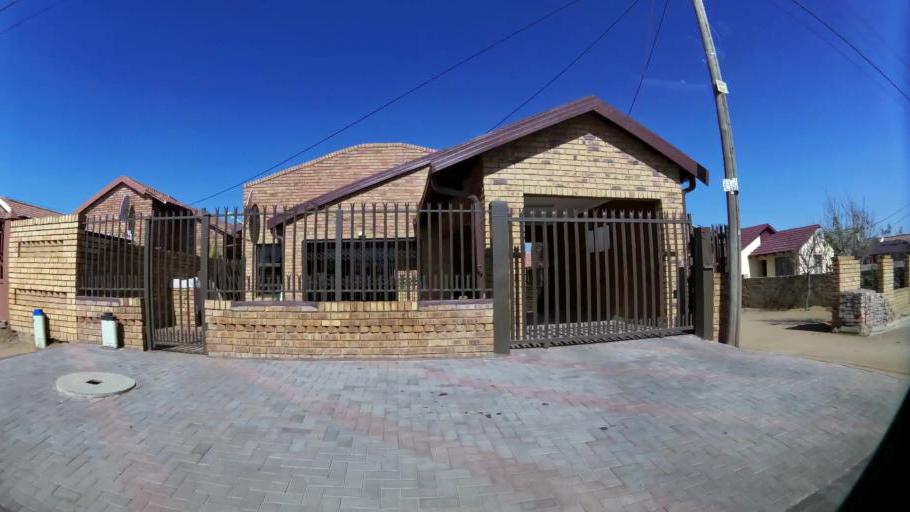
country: ZA
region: Gauteng
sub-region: City of Tshwane Metropolitan Municipality
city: Mabopane
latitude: -25.5543
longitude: 28.0766
